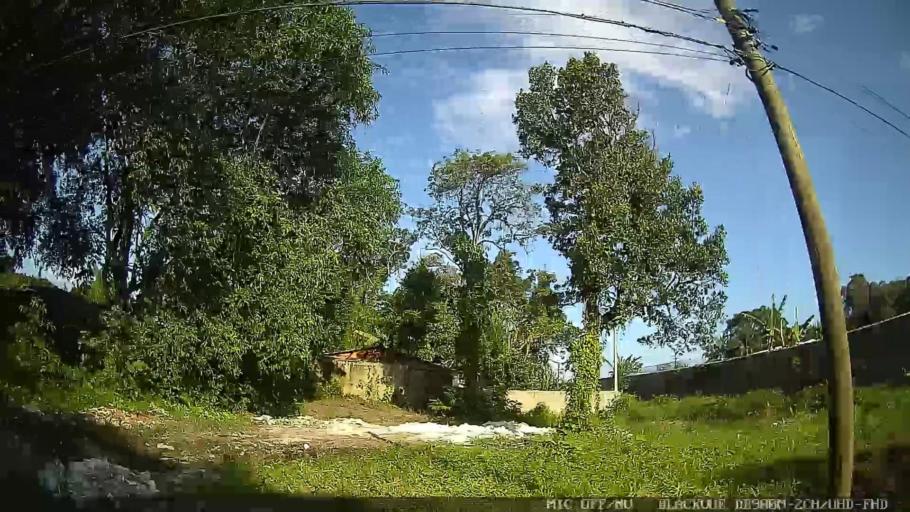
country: BR
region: Sao Paulo
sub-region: Itanhaem
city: Itanhaem
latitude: -24.1766
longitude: -46.8250
